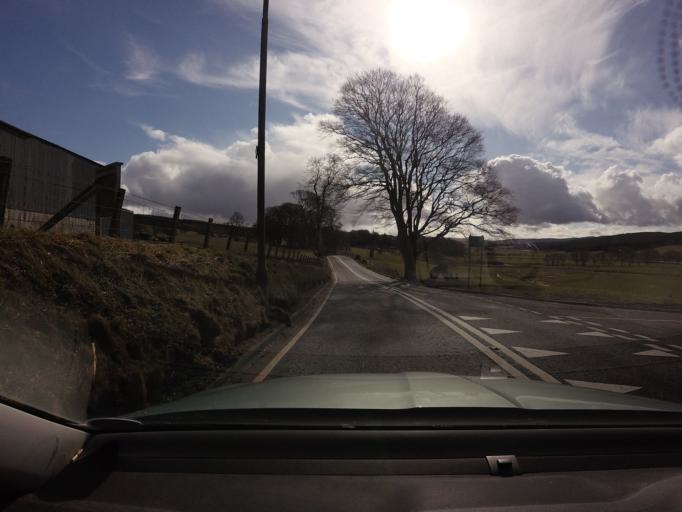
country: GB
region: Scotland
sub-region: South Lanarkshire
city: Douglas
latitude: 55.5524
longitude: -3.8509
